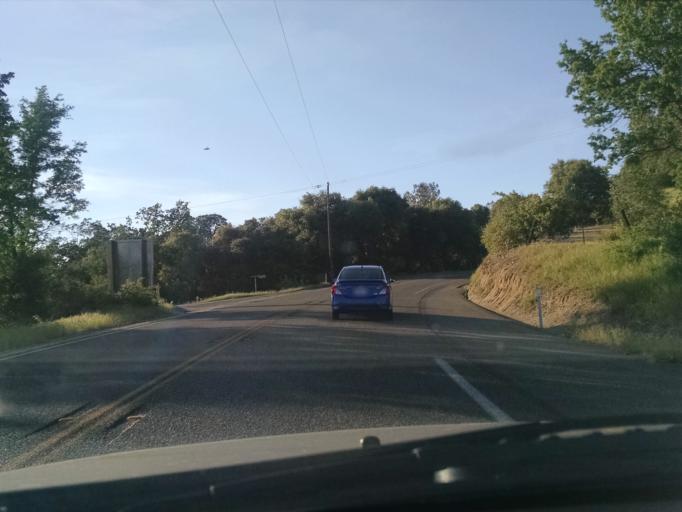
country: US
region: California
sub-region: Madera County
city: Ahwahnee
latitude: 37.3854
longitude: -119.7372
